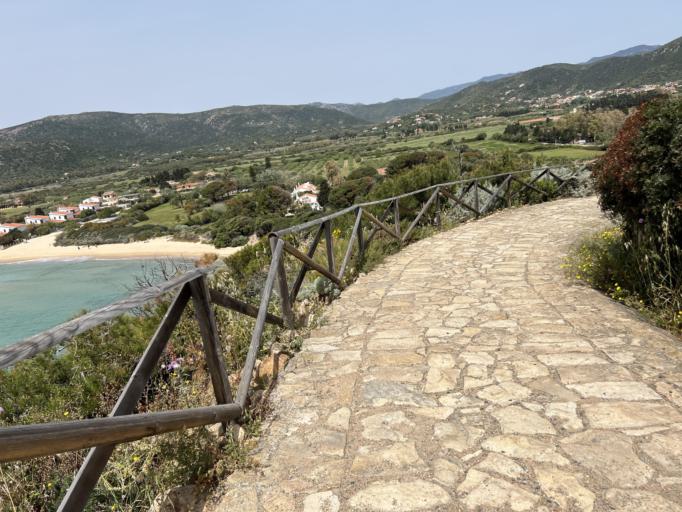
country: IT
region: Sardinia
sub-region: Provincia di Cagliari
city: Domus de Maria
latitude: 38.8953
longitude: 8.8842
